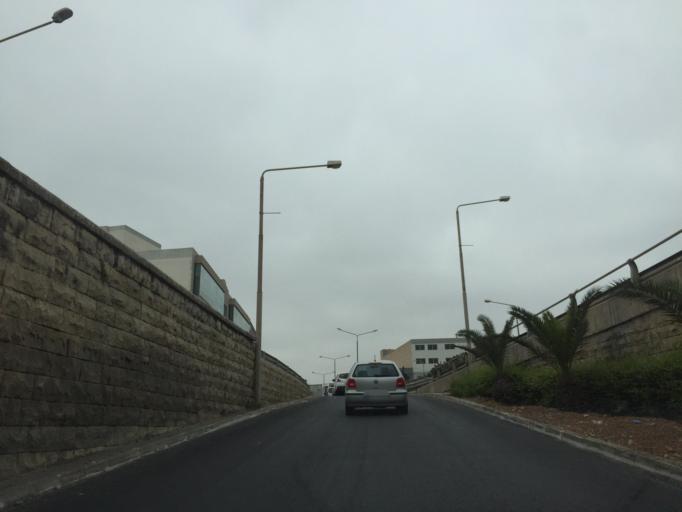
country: MT
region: Il-Hamrun
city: Hamrun
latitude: 35.8848
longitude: 14.4787
